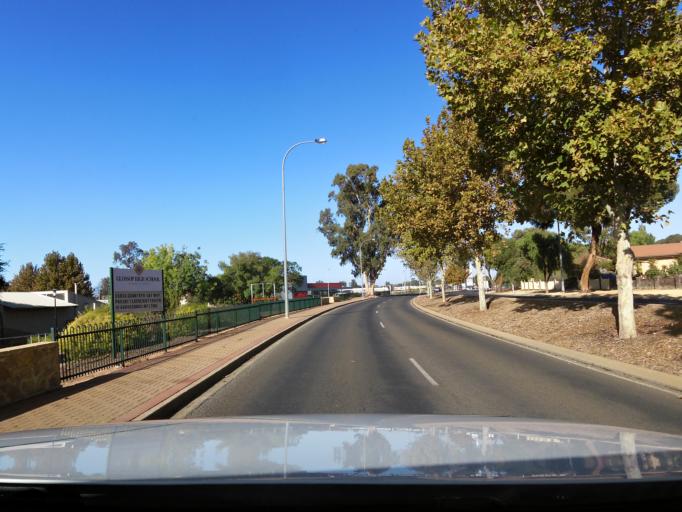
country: AU
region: South Australia
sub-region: Berri and Barmera
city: Berri
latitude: -34.2776
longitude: 140.6099
